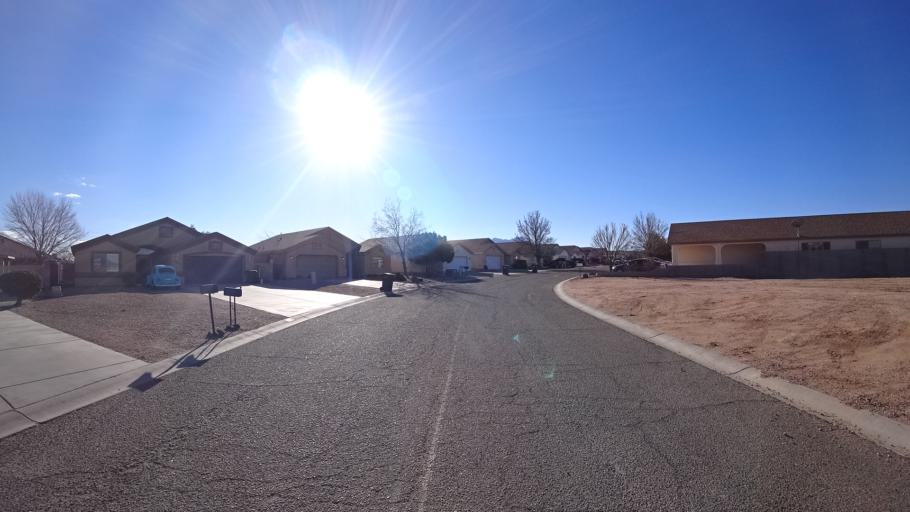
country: US
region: Arizona
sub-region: Mohave County
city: New Kingman-Butler
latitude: 35.2243
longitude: -113.9961
